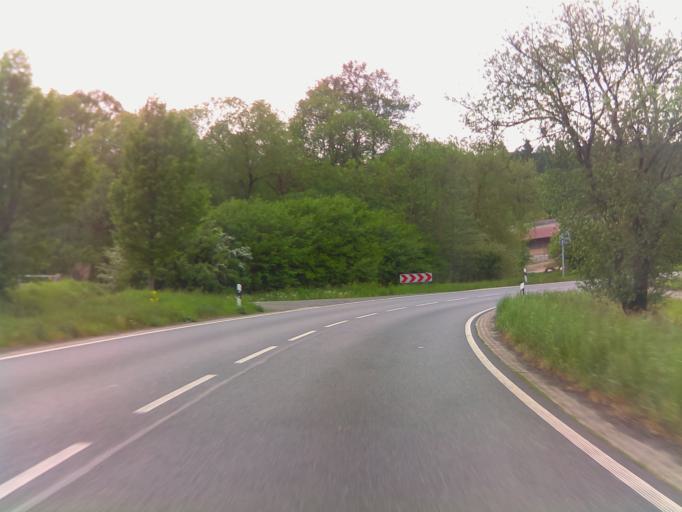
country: DE
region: Hesse
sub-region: Regierungsbezirk Kassel
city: Jesberg
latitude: 50.9782
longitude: 9.1168
